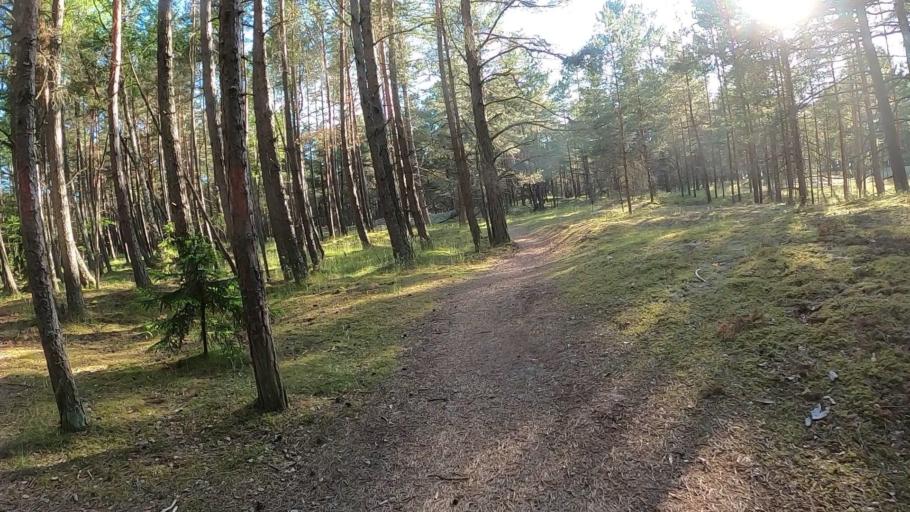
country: LV
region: Carnikava
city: Carnikava
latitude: 57.1348
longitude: 24.2336
